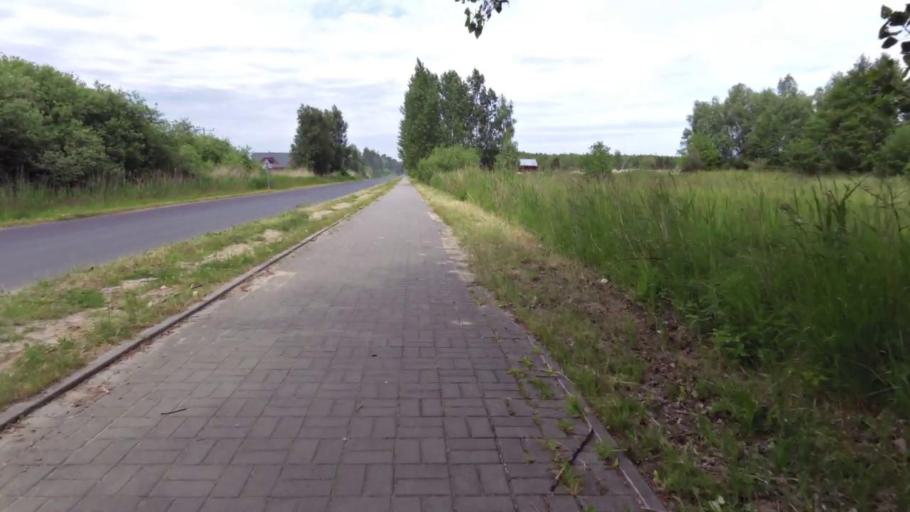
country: PL
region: West Pomeranian Voivodeship
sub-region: Powiat kamienski
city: Dziwnow
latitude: 53.9932
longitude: 14.6856
